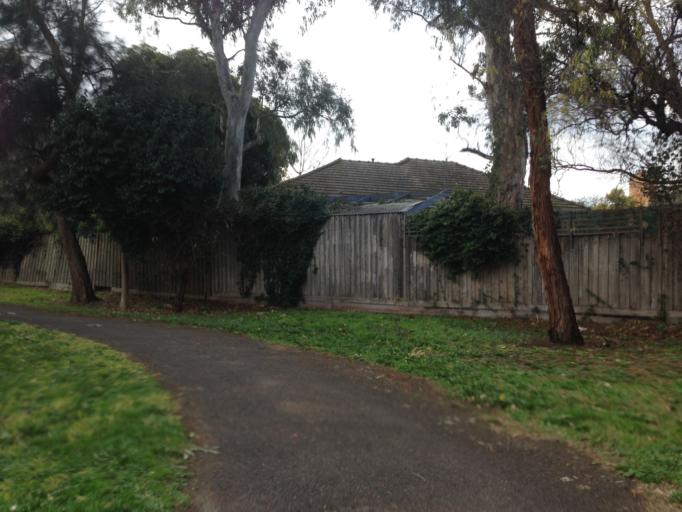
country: AU
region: Victoria
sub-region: Banyule
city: Bellfield
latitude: -37.7631
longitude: 145.0388
